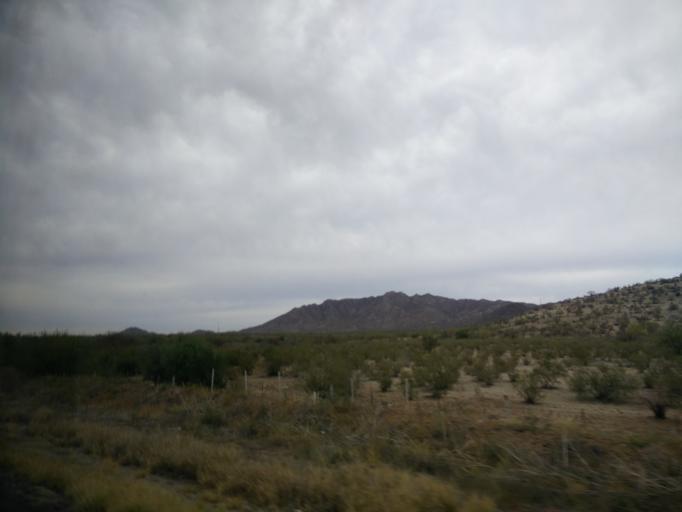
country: MX
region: Sonora
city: Hermosillo
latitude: 28.9405
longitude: -110.9594
